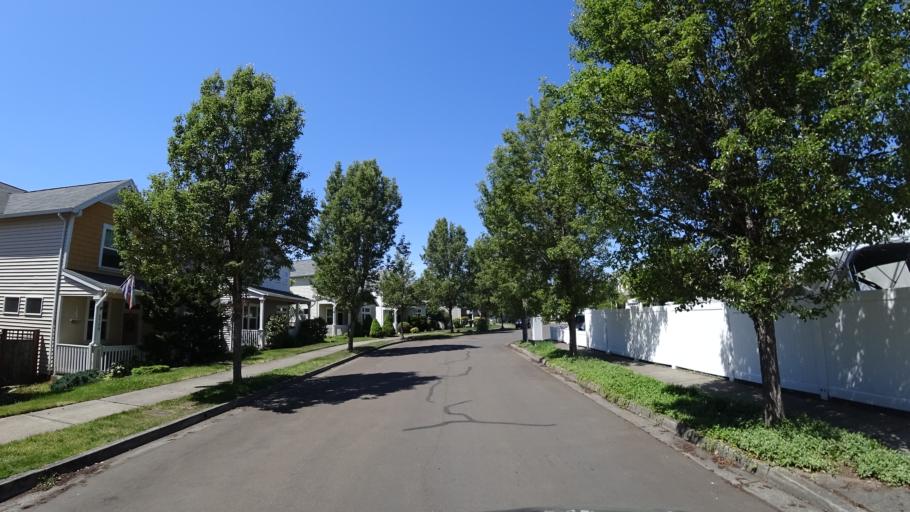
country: US
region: Oregon
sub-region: Washington County
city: Rockcreek
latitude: 45.5238
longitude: -122.9235
